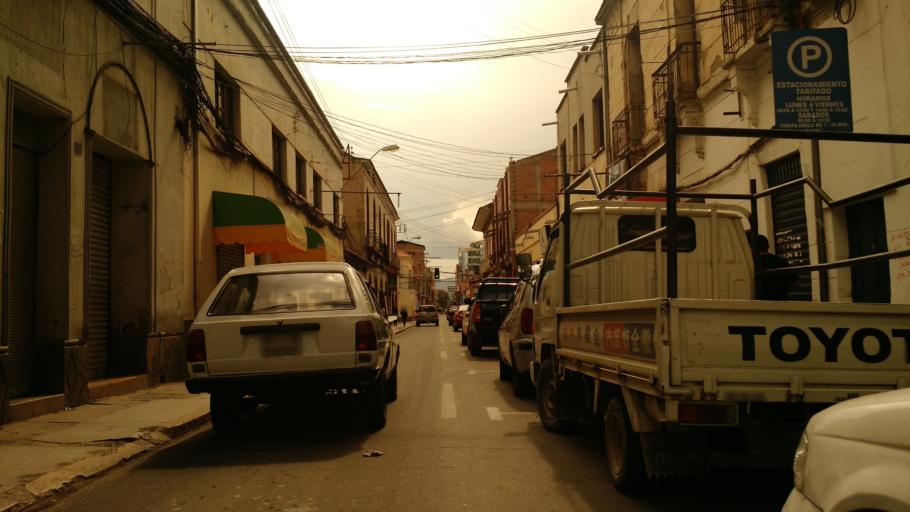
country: BO
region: Cochabamba
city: Cochabamba
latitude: -17.3936
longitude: -66.1589
